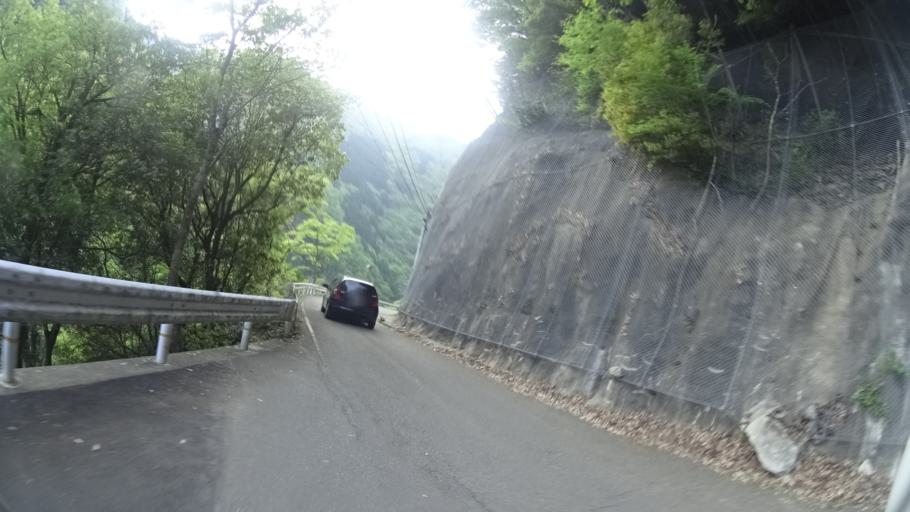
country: JP
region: Tokushima
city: Ikedacho
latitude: 33.9038
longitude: 133.8133
